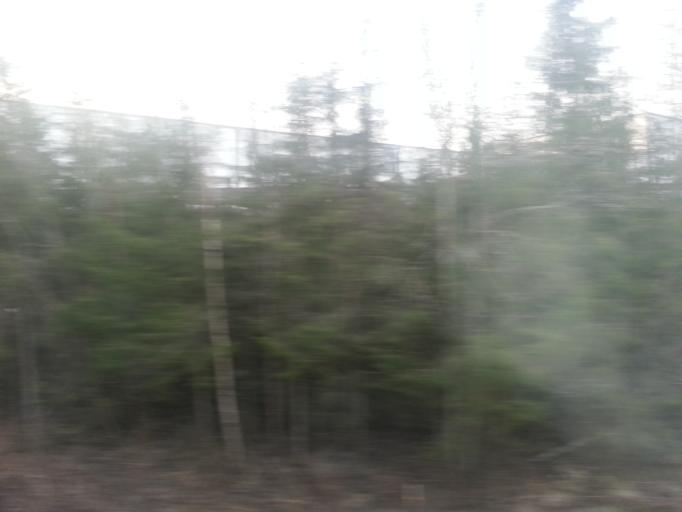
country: NO
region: Sor-Trondelag
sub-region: Trondheim
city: Trondheim
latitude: 63.3462
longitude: 10.3537
